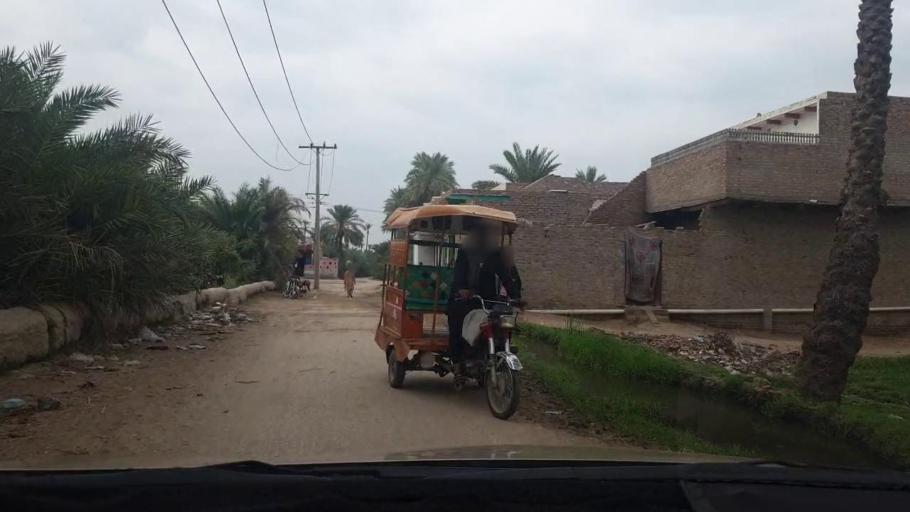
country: PK
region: Sindh
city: Larkana
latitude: 27.5652
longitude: 68.2299
